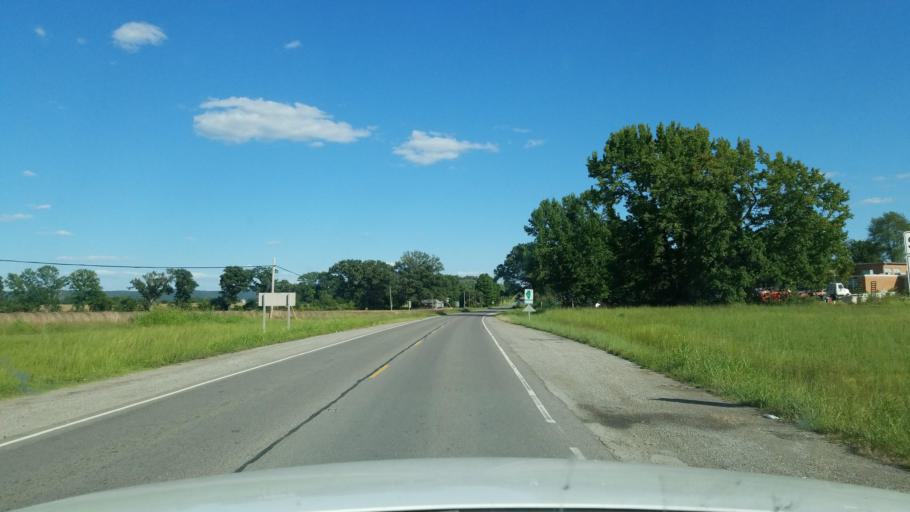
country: US
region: Illinois
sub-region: Saline County
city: Harrisburg
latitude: 37.6413
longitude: -88.5319
